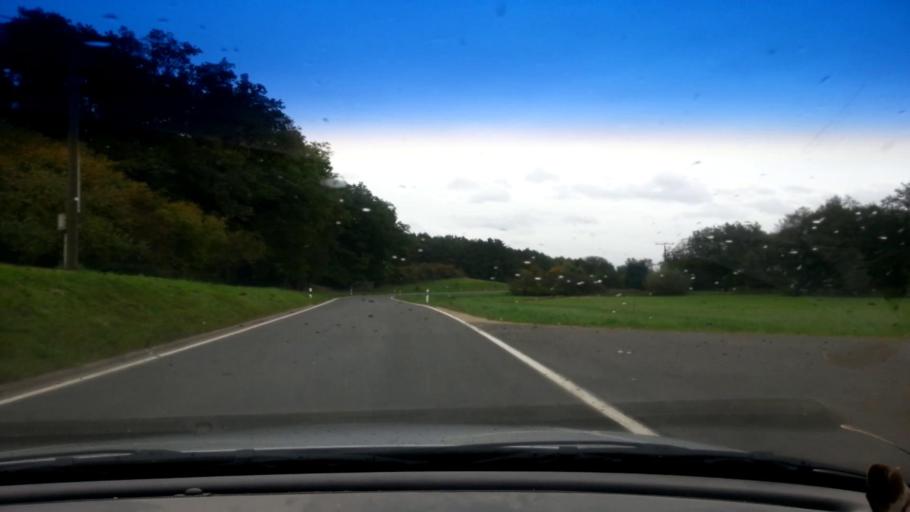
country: DE
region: Bavaria
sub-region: Upper Franconia
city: Lauter
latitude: 49.9881
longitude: 10.7603
